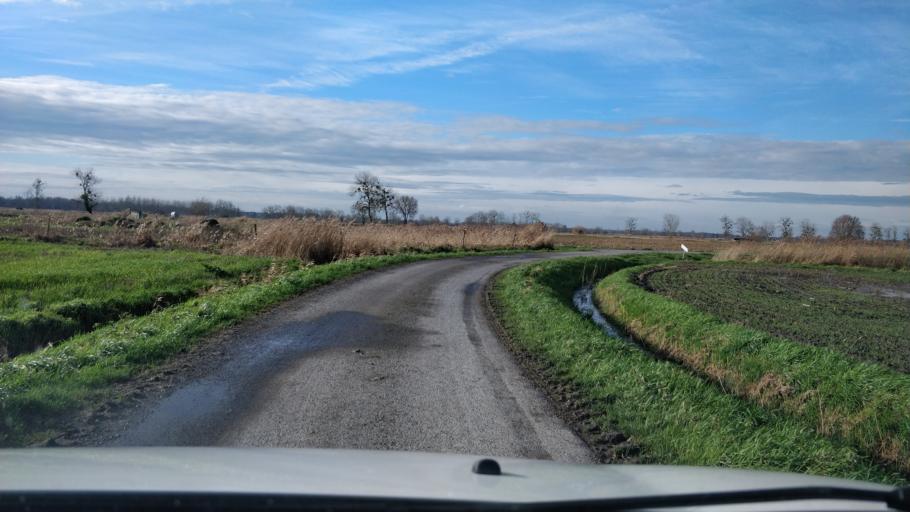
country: FR
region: Brittany
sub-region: Departement d'Ille-et-Vilaine
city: La Fresnais
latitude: 48.5755
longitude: -1.8219
